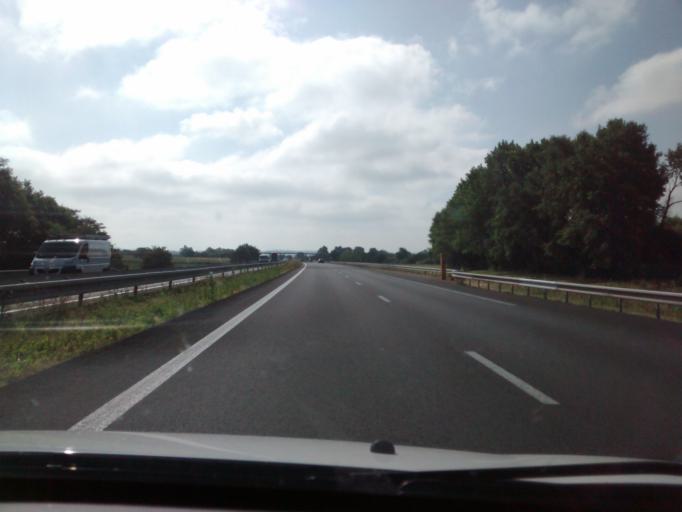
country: FR
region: Pays de la Loire
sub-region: Departement de la Mayenne
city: Sainte-Suzanne
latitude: 48.0274
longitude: -0.3424
